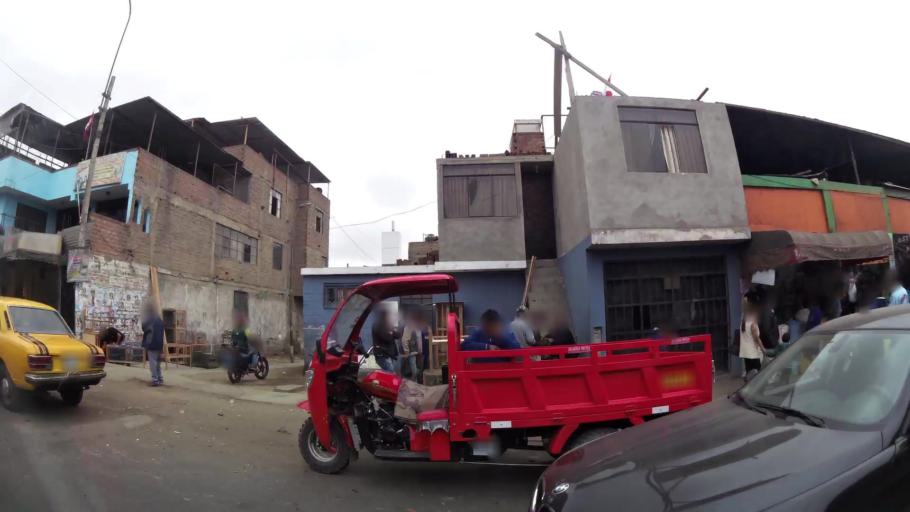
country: PE
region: Lima
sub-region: Lima
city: Surco
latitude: -12.1504
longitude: -76.9690
